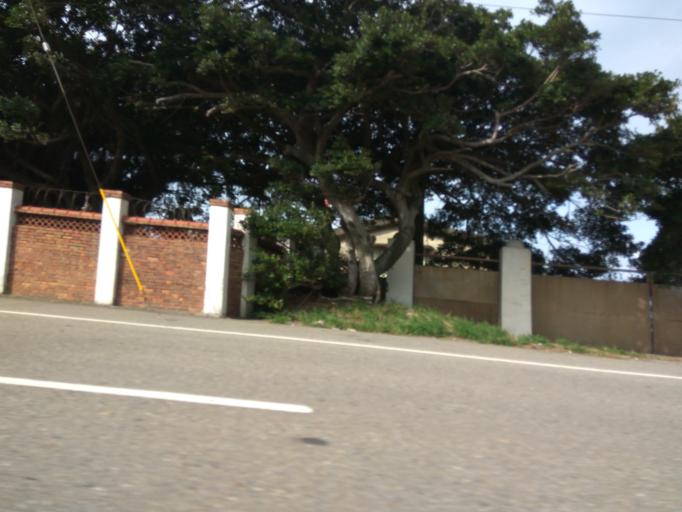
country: TW
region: Taiwan
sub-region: Hsinchu
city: Zhubei
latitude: 24.9828
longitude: 121.0268
